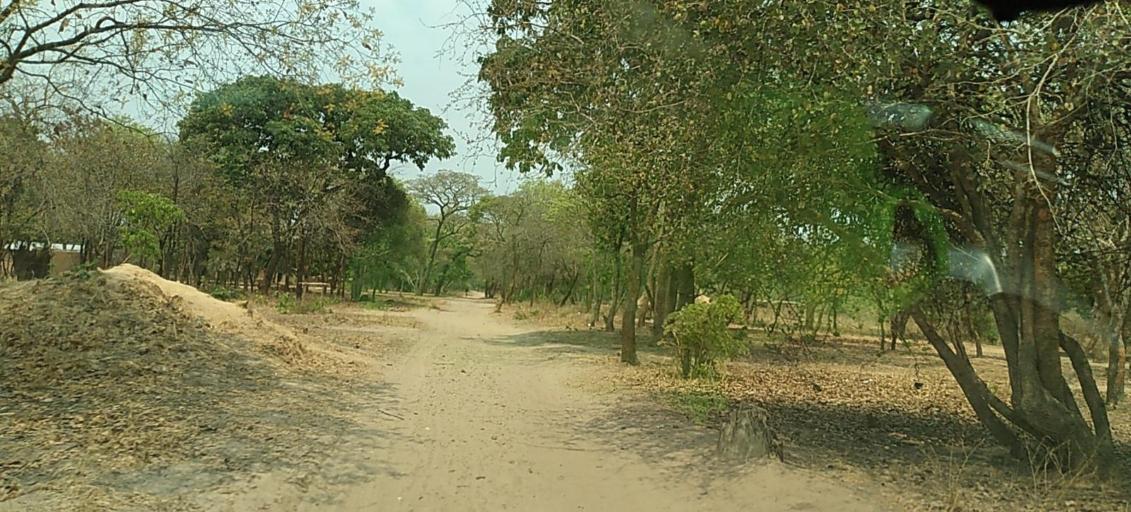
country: ZM
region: North-Western
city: Kabompo
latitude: -13.5579
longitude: 24.4469
